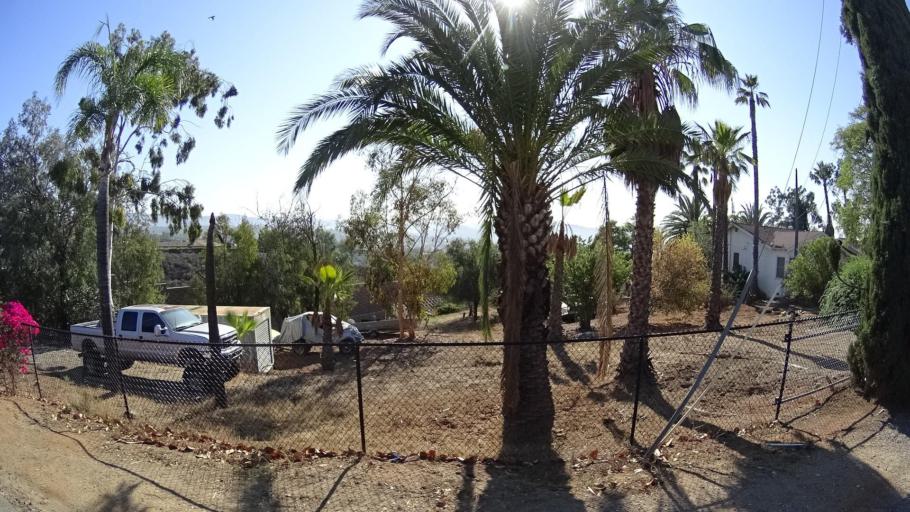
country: US
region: California
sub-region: San Diego County
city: Escondido
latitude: 33.0858
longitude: -117.0772
